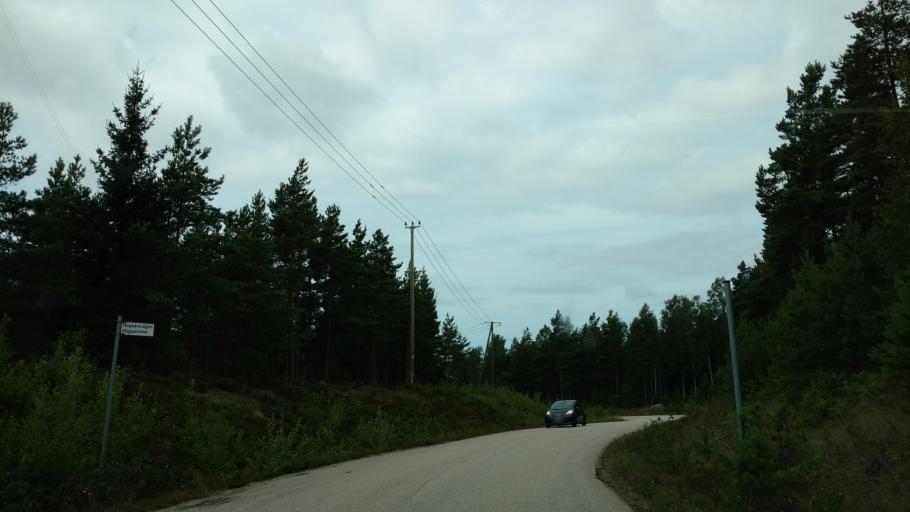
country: FI
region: Varsinais-Suomi
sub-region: Aboland-Turunmaa
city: Dragsfjaerd
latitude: 59.9465
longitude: 22.4135
